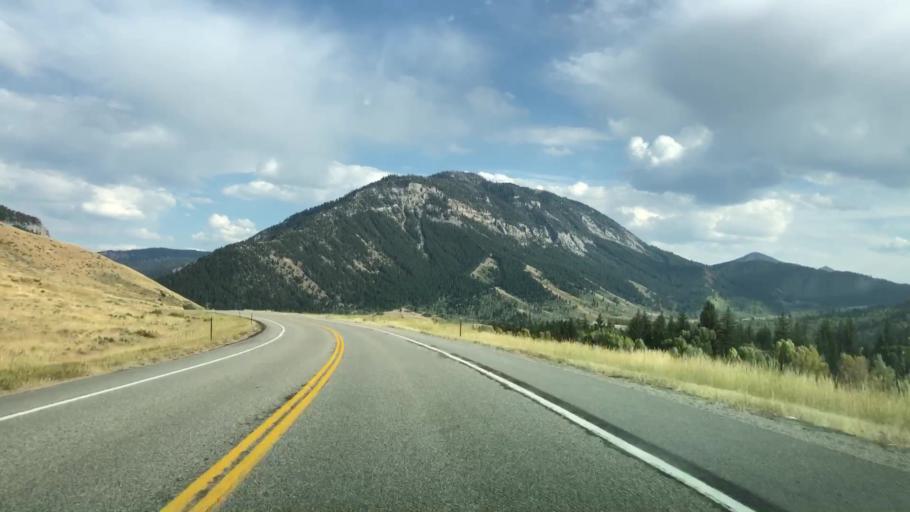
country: US
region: Wyoming
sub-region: Teton County
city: Hoback
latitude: 43.2963
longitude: -110.6629
